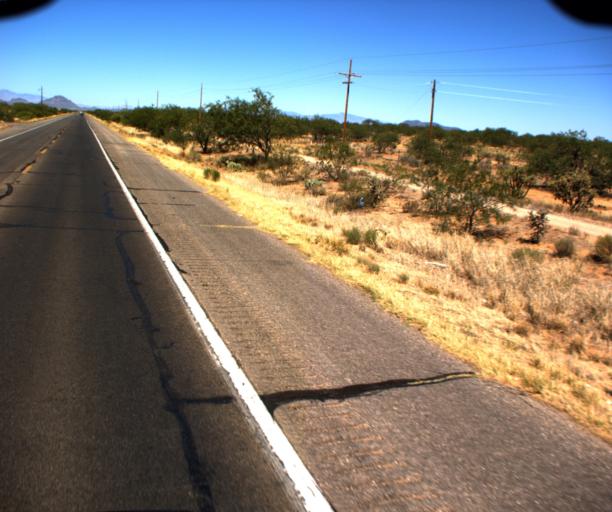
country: US
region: Arizona
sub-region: Pima County
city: Three Points
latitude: 32.1010
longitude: -111.2524
